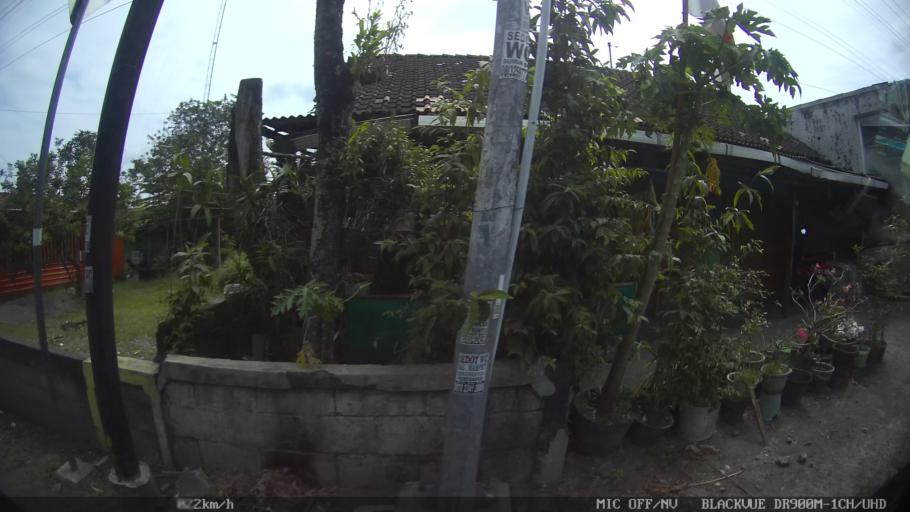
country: ID
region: Central Java
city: Candi Prambanan
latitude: -7.7544
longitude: 110.4807
